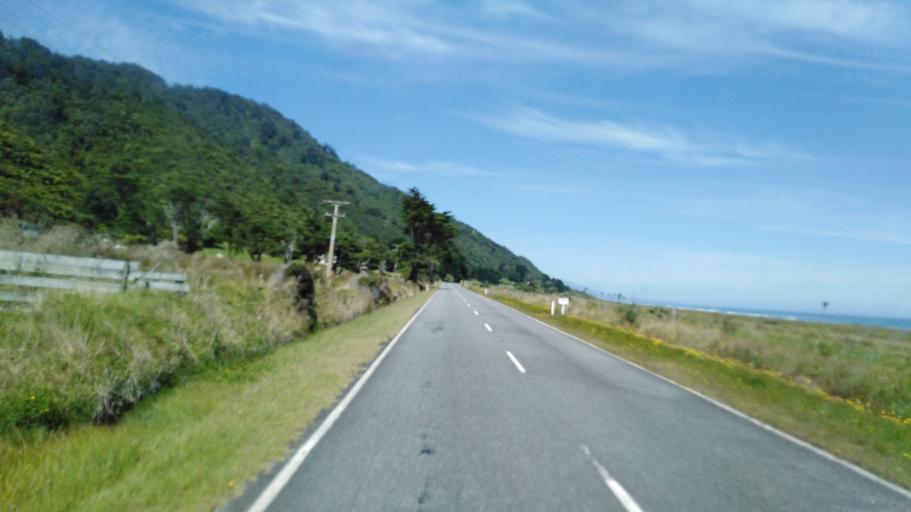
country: NZ
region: West Coast
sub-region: Buller District
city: Westport
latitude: -41.5600
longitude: 171.9165
